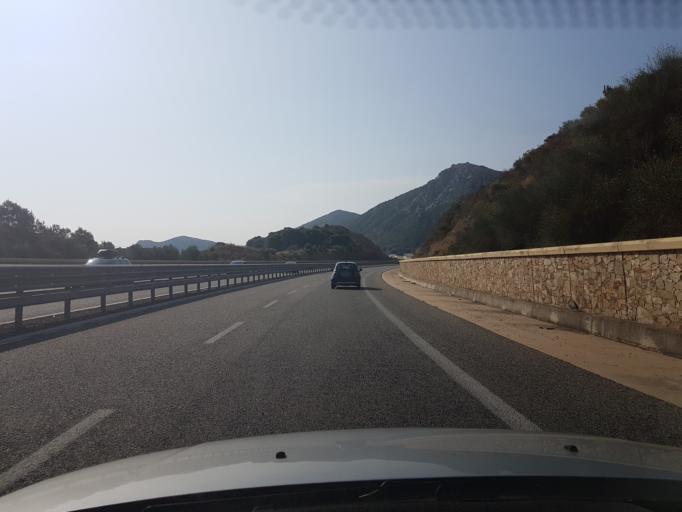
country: IT
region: Sardinia
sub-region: Provincia di Olbia-Tempio
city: San Teodoro
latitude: 40.7953
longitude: 9.6083
